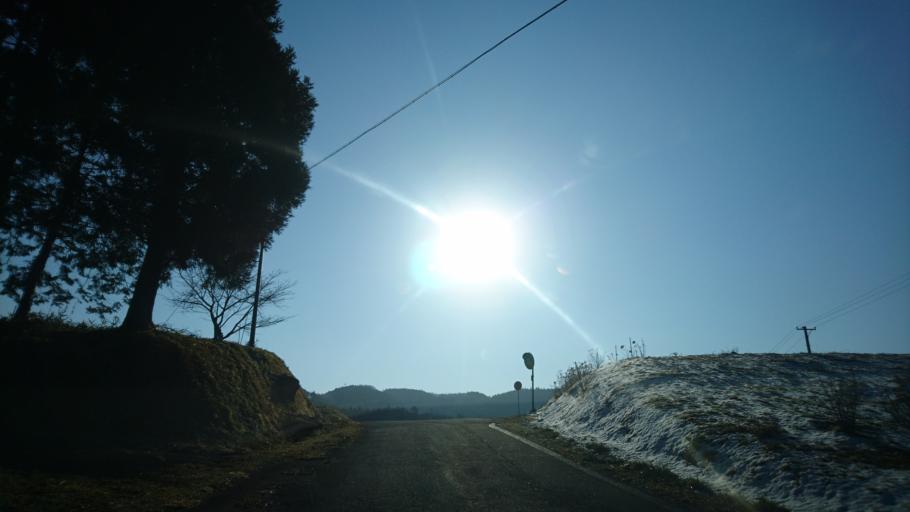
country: JP
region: Iwate
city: Ichinoseki
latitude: 38.9173
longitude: 141.2892
